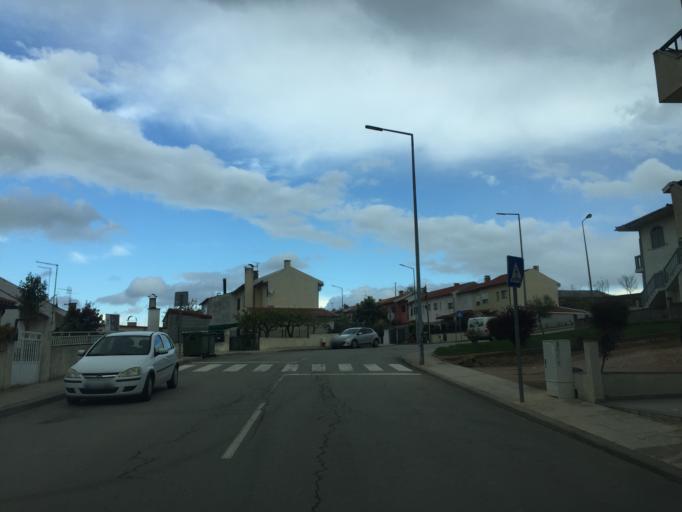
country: PT
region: Braganca
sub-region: Mogadouro
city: Mogadouro
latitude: 41.3437
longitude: -6.7033
